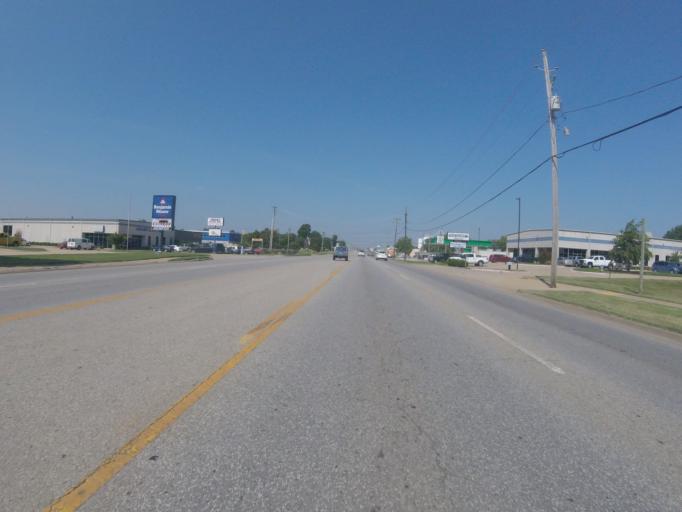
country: US
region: Arkansas
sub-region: Washington County
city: Springdale
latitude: 36.1671
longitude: -94.1287
